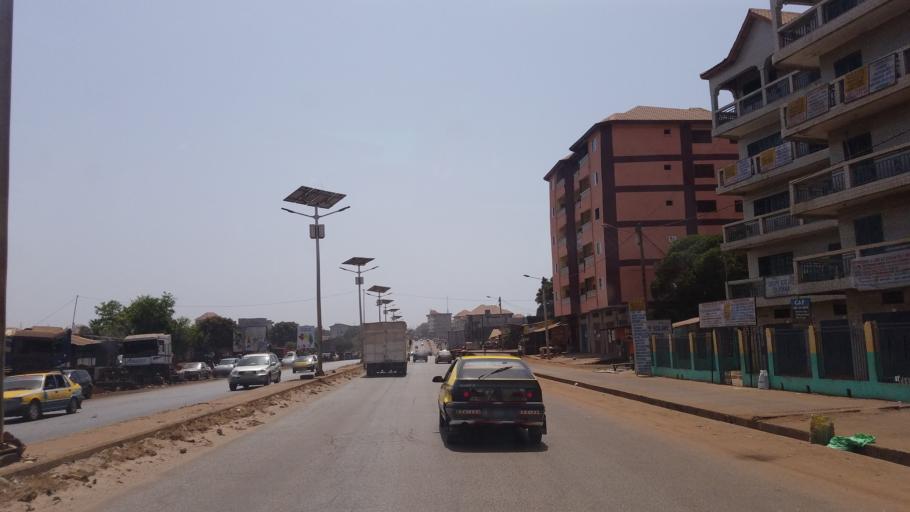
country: GN
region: Conakry
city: Conakry
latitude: 9.6511
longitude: -13.5807
